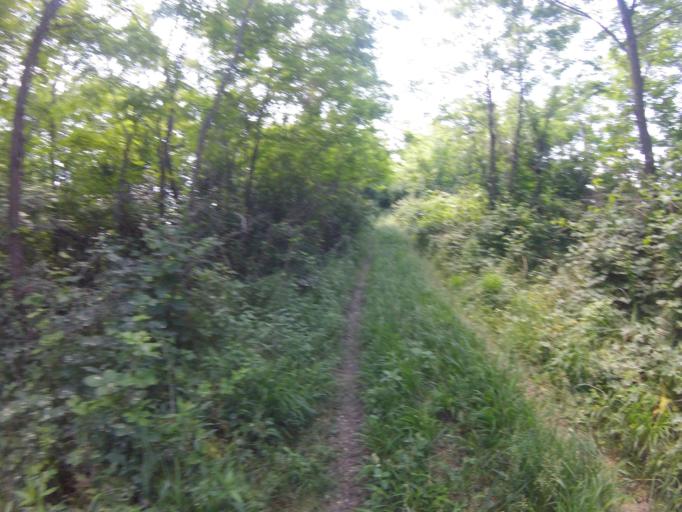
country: HU
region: Zala
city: Zalaszentgrot
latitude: 46.9085
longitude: 17.0411
